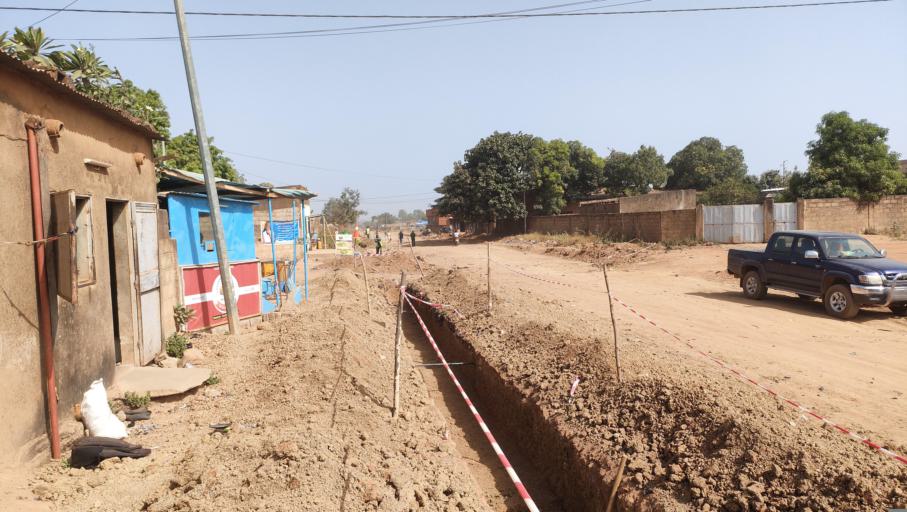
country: BF
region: Est
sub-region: Province du Gourma
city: Fada N'gourma
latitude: 12.0606
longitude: 0.3723
